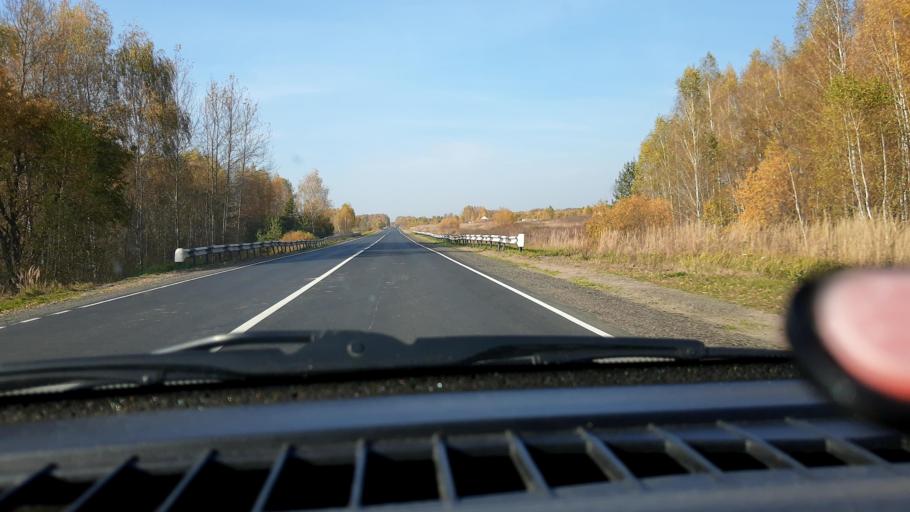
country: RU
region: Nizjnij Novgorod
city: Novaya Balakhna
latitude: 56.5819
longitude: 43.6844
